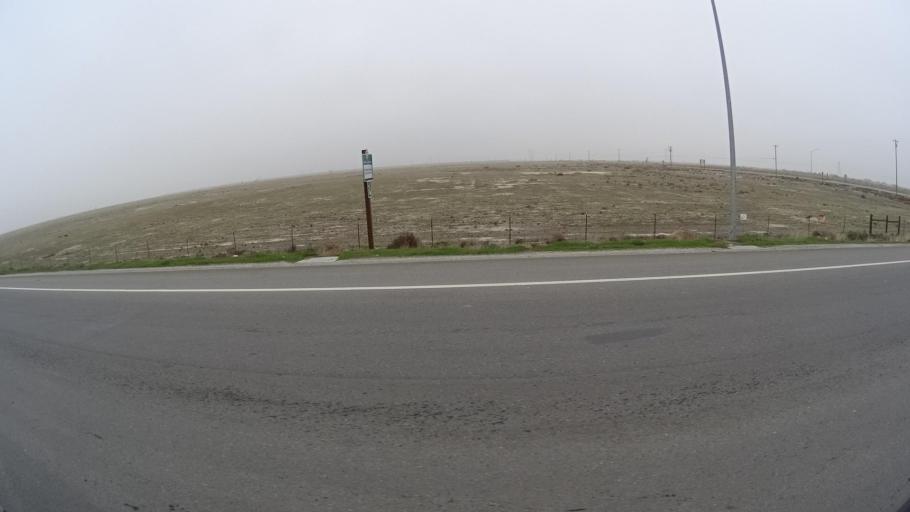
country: US
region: California
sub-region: Kern County
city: Rosedale
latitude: 35.2674
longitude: -119.2539
